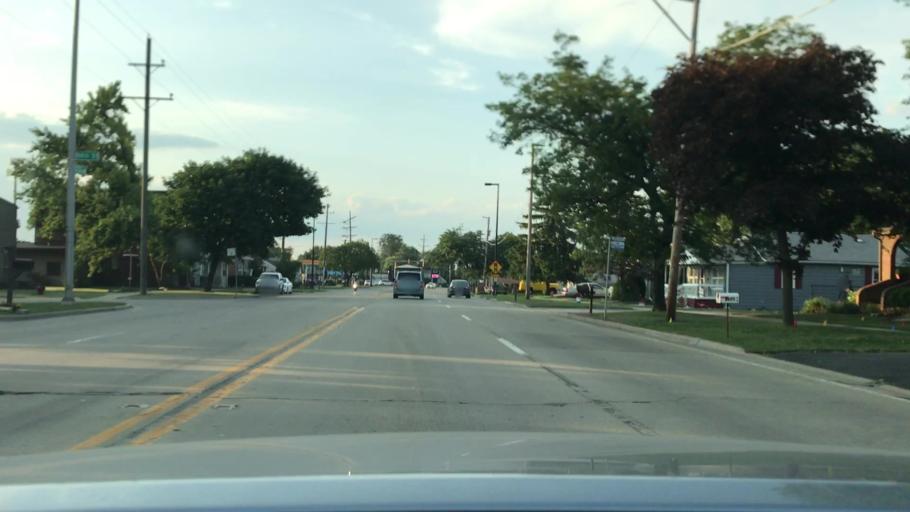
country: US
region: Illinois
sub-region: Cook County
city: Burbank
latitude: 41.7321
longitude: -87.7607
